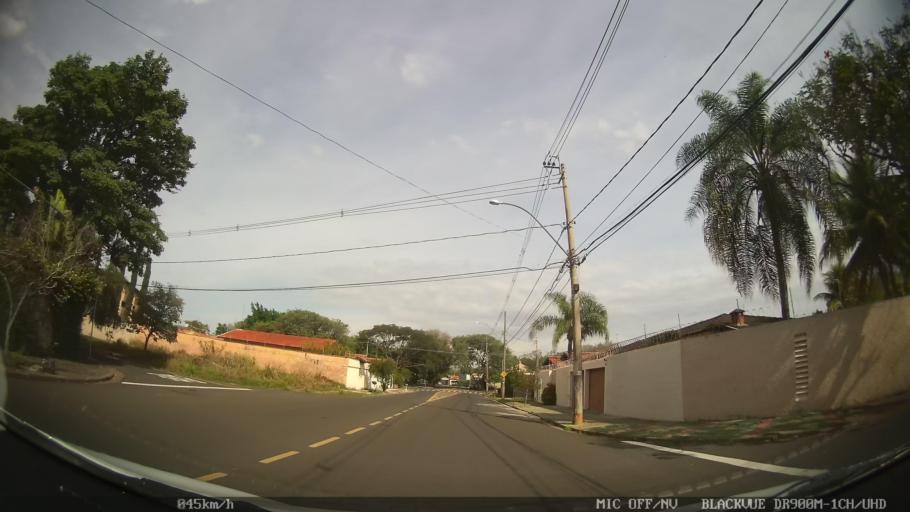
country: BR
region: Sao Paulo
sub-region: Piracicaba
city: Piracicaba
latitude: -22.7116
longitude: -47.6732
